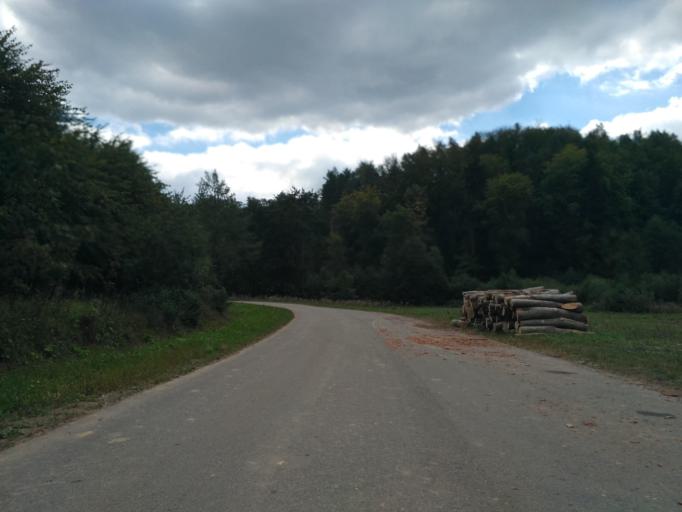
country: PL
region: Subcarpathian Voivodeship
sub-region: Powiat rzeszowski
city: Dynow
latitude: 49.7680
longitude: 22.2655
